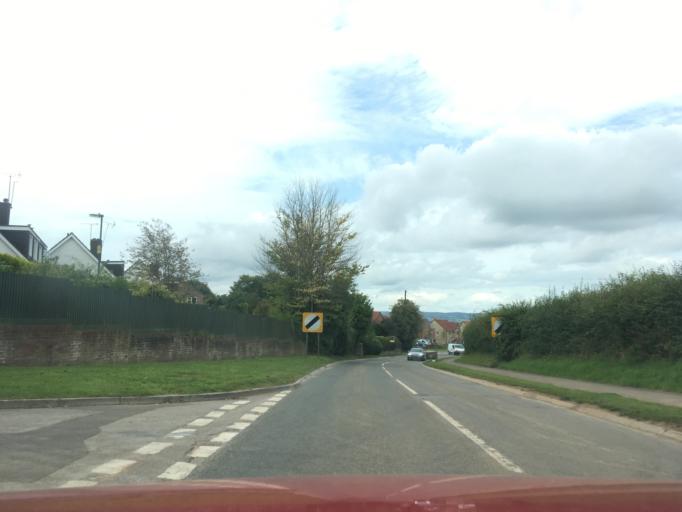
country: GB
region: England
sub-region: South Gloucestershire
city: Thornbury
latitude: 51.6196
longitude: -2.5180
